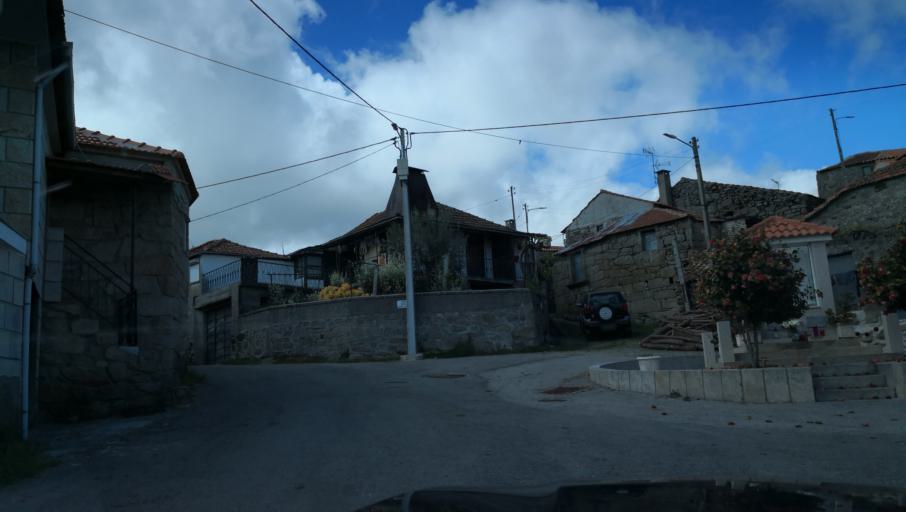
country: PT
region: Vila Real
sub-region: Vila Real
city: Vila Real
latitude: 41.4073
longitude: -7.7132
